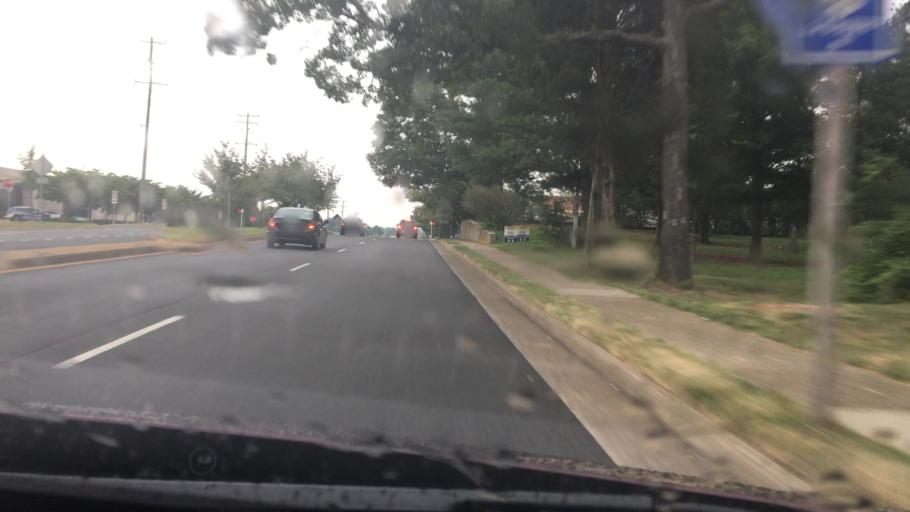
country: US
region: Virginia
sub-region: City of Fairfax
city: Fairfax
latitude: 38.8545
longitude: -77.3284
